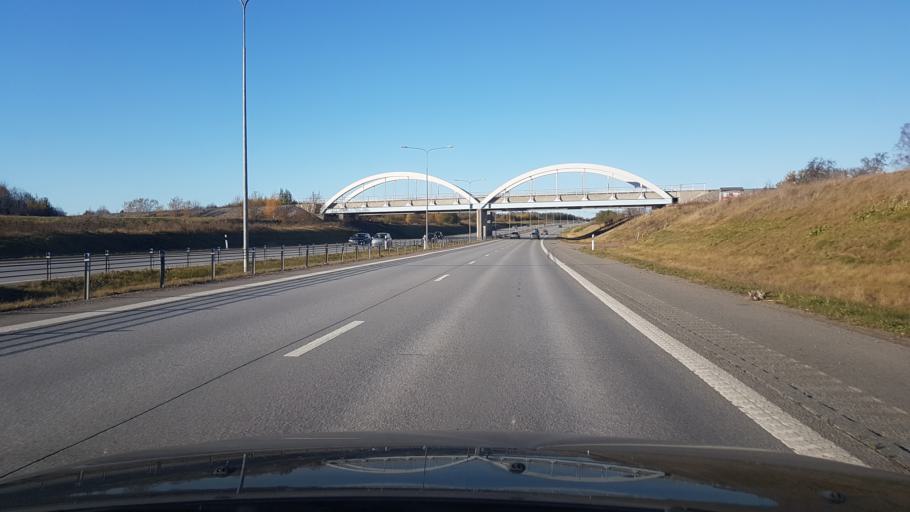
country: SE
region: Uppsala
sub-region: Uppsala Kommun
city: Saevja
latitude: 59.8662
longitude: 17.7131
